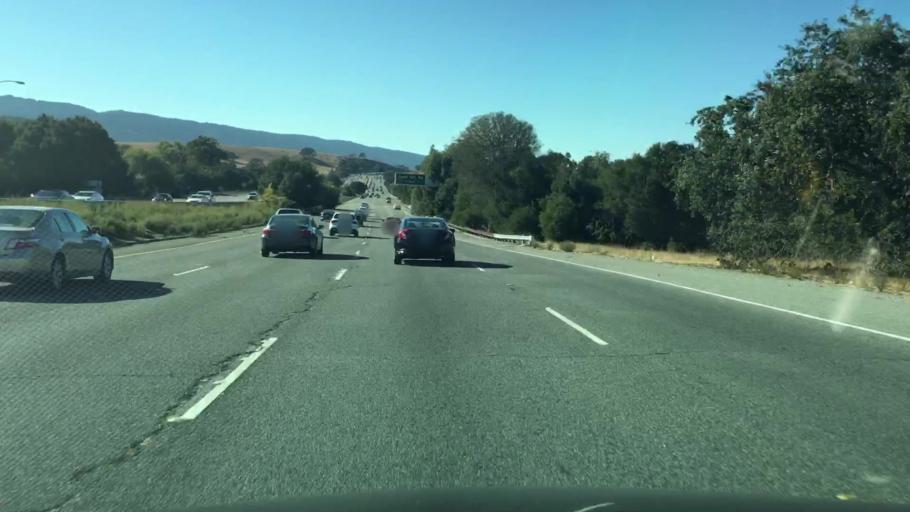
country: US
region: California
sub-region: San Mateo County
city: Ladera
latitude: 37.4085
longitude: -122.1923
